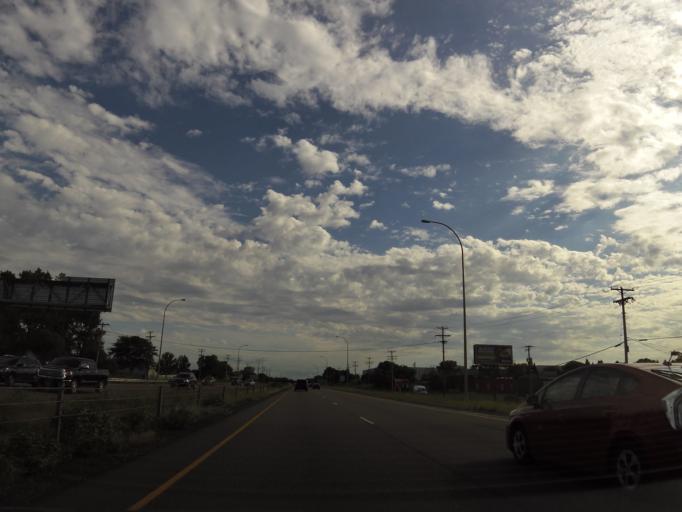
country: US
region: Minnesota
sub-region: Hennepin County
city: New Hope
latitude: 45.0539
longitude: -93.4010
